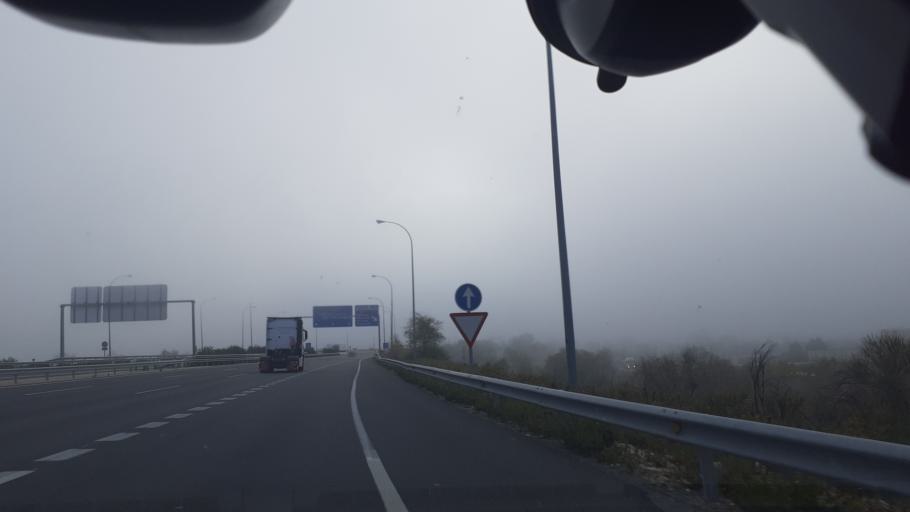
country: ES
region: Madrid
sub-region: Provincia de Madrid
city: Vicalvaro
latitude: 40.3953
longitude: -3.5779
